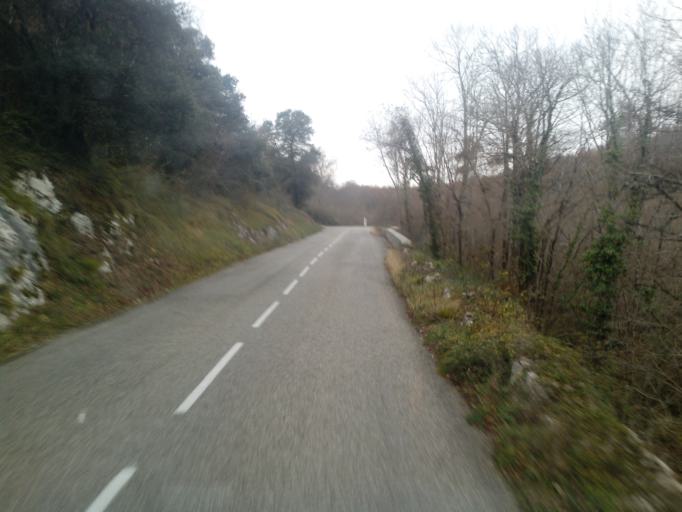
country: FR
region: Midi-Pyrenees
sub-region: Departement de l'Ariege
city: Foix
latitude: 43.0304
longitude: 1.5379
